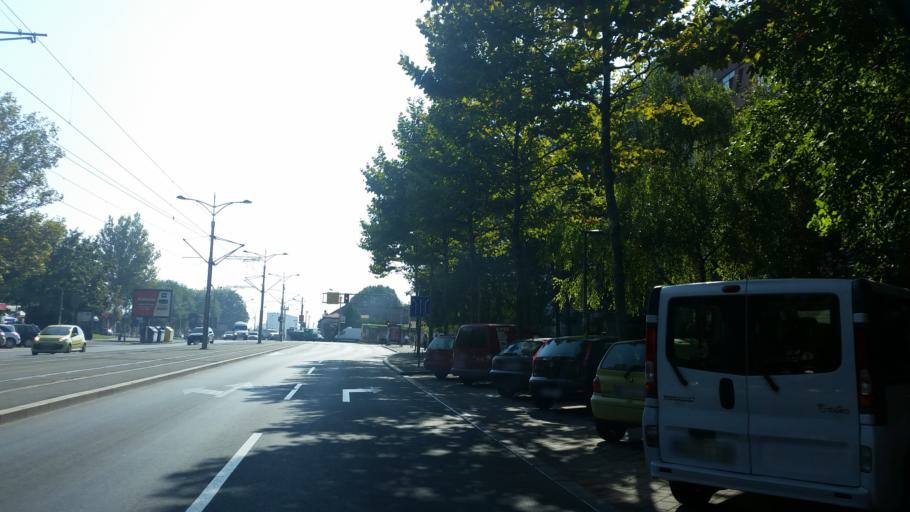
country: RS
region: Central Serbia
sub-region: Belgrade
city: Palilula
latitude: 44.7939
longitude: 20.5025
